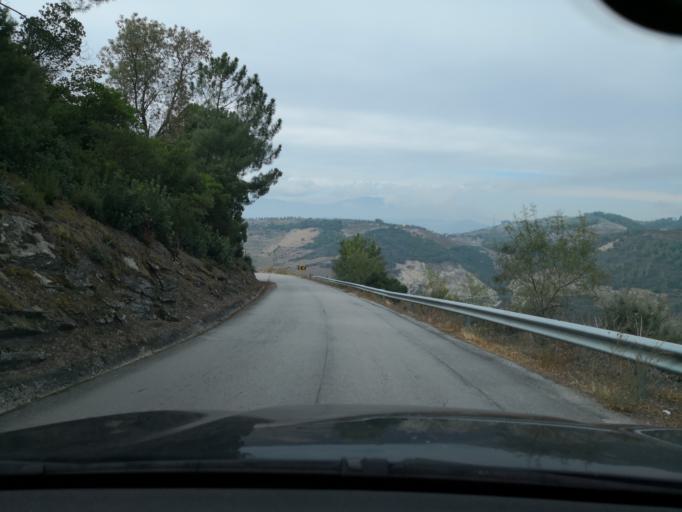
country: PT
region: Vila Real
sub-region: Peso da Regua
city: Peso da Regua
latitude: 41.1982
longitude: -7.7292
